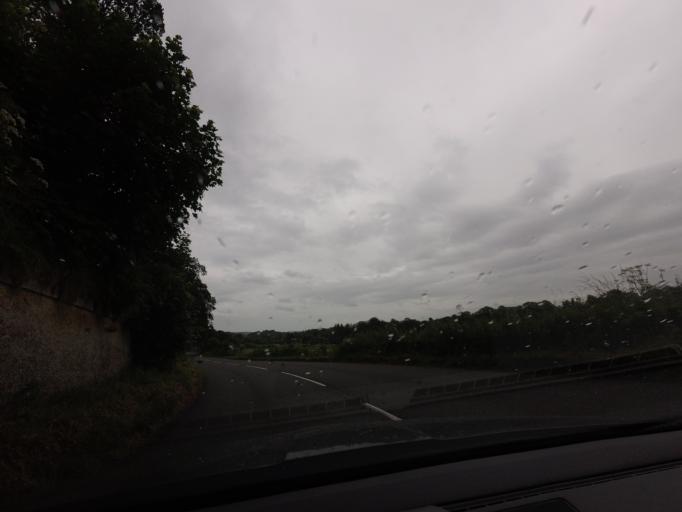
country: GB
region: Scotland
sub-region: Aberdeenshire
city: Turriff
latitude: 57.5385
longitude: -2.4987
